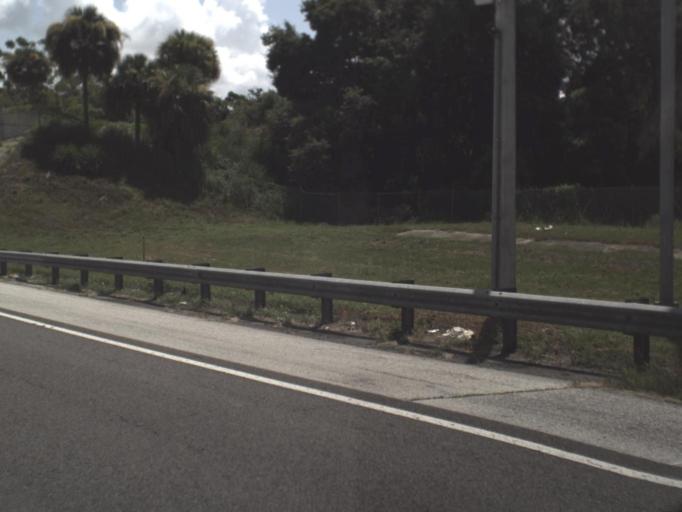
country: US
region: Florida
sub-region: Hillsborough County
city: Mango
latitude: 28.0029
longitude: -82.3197
